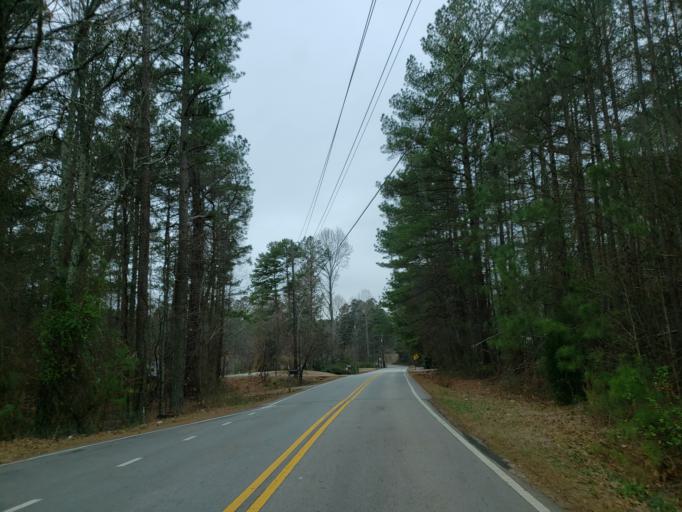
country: US
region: Georgia
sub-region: Paulding County
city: Hiram
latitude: 33.9367
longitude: -84.7142
